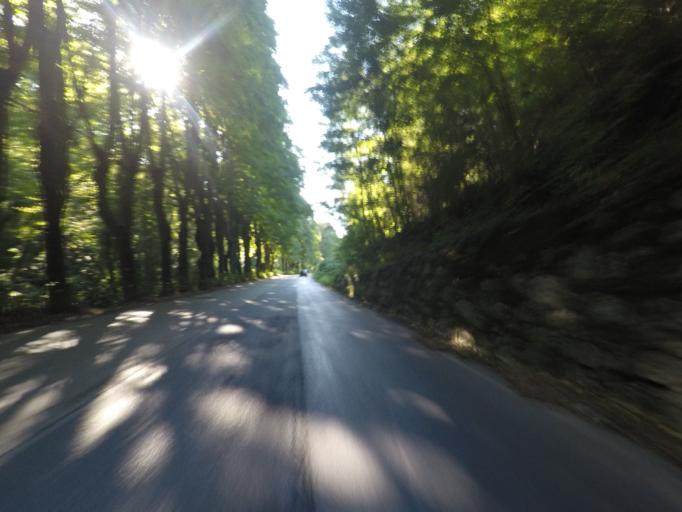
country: IT
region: Tuscany
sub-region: Provincia di Lucca
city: Massarosa
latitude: 43.9037
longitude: 10.3721
